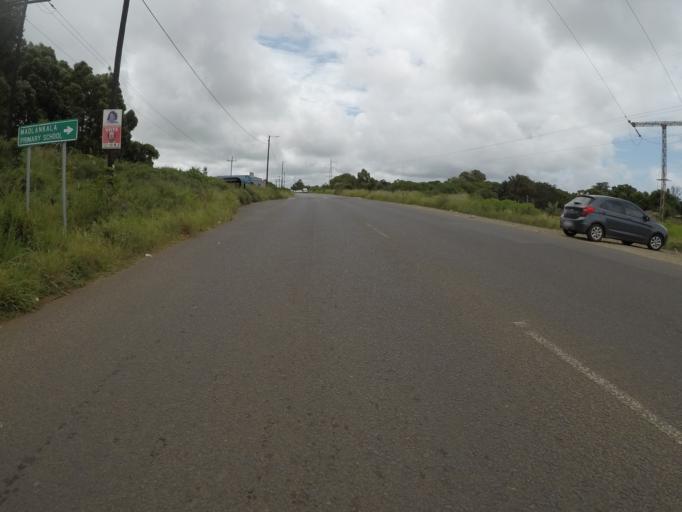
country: ZA
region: KwaZulu-Natal
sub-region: uThungulu District Municipality
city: eSikhawini
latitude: -28.8454
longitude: 31.9320
